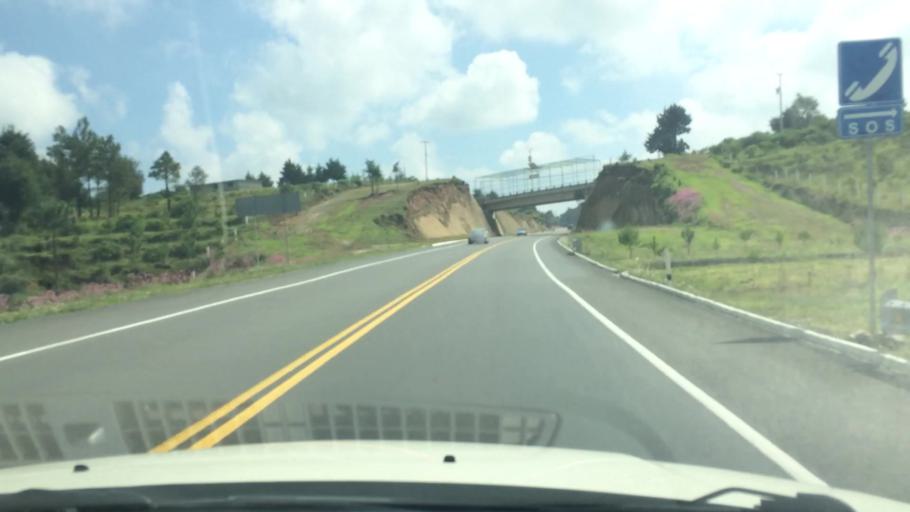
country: MX
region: Mexico
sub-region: Villa Victoria
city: Colonia Doctor Gustavo Baz
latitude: 19.3615
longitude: -99.9522
